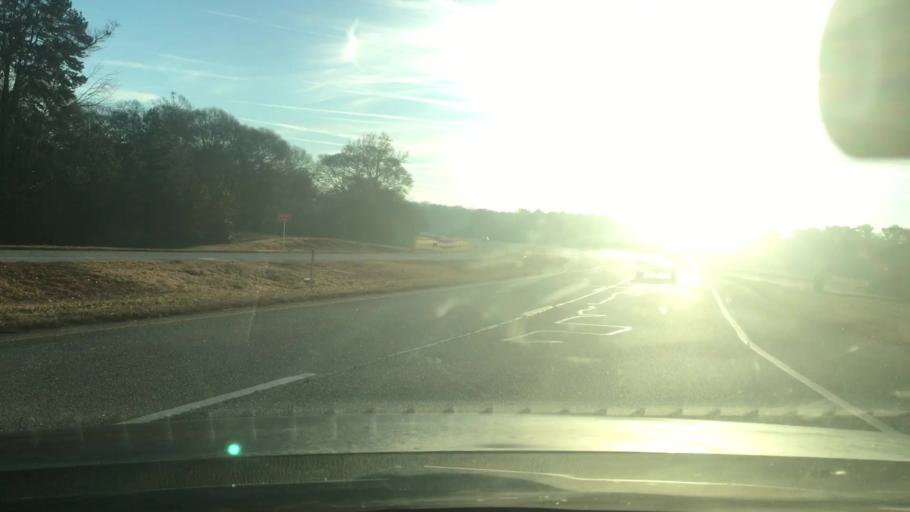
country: US
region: Georgia
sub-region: Spalding County
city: Experiment
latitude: 33.2758
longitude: -84.3157
